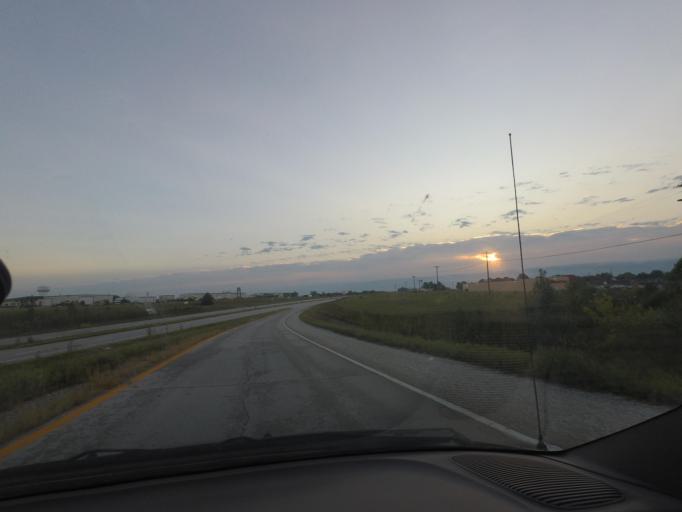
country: US
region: Missouri
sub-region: Macon County
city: Macon
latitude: 39.7540
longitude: -92.4672
